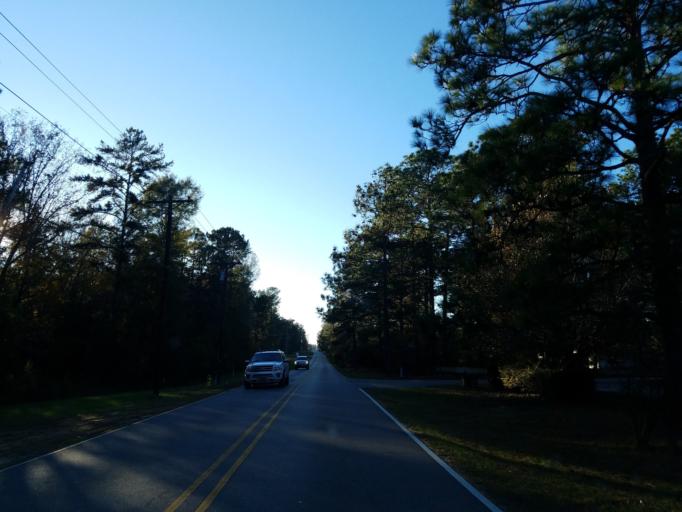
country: US
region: Mississippi
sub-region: Lamar County
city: Arnold Line
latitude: 31.3467
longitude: -89.3821
